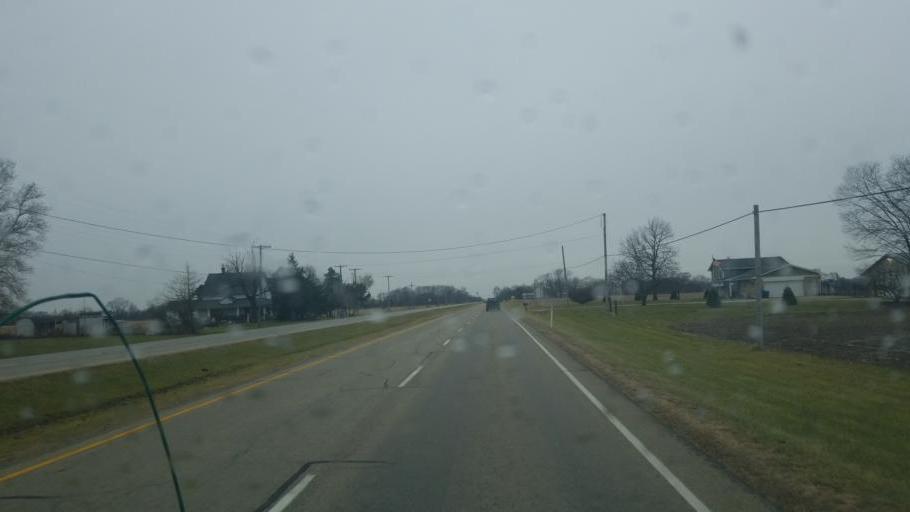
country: US
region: Indiana
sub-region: Henry County
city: Knightstown
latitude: 39.7908
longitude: -85.6344
